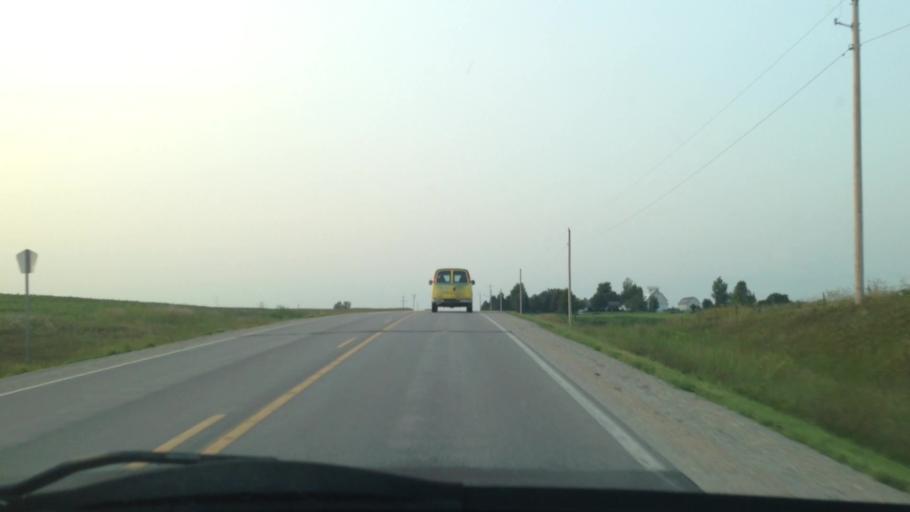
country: US
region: Iowa
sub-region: Benton County
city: Atkins
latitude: 42.0186
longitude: -91.8738
